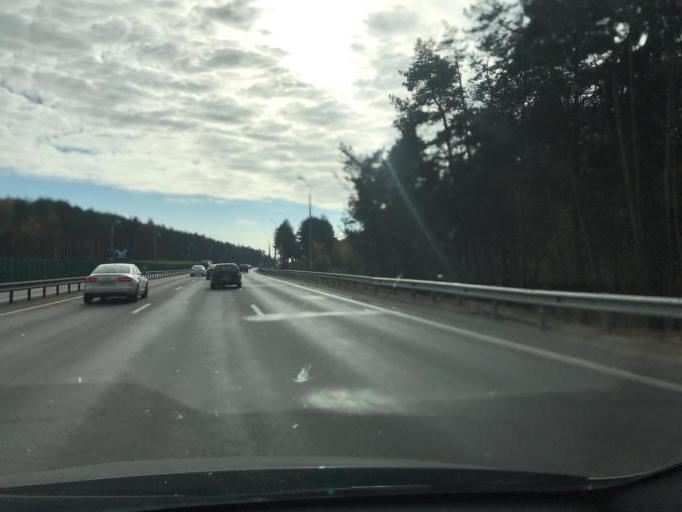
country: BY
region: Minsk
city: Vyaliki Trastsyanets
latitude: 53.8806
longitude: 27.6967
